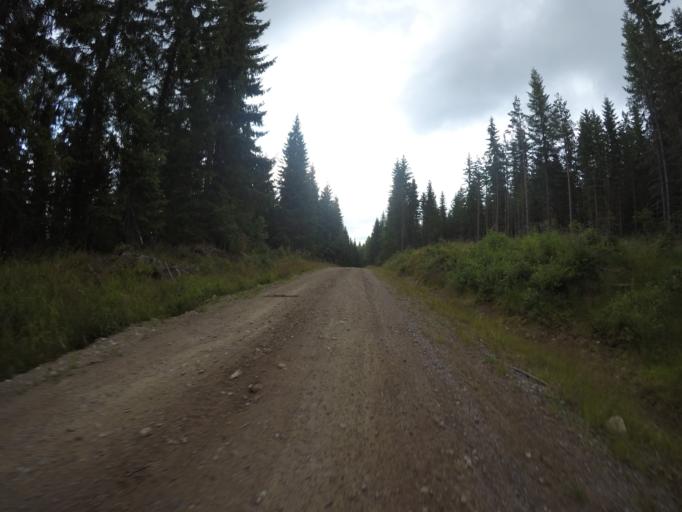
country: SE
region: Vaermland
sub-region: Filipstads Kommun
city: Lesjofors
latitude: 60.1990
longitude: 14.3805
